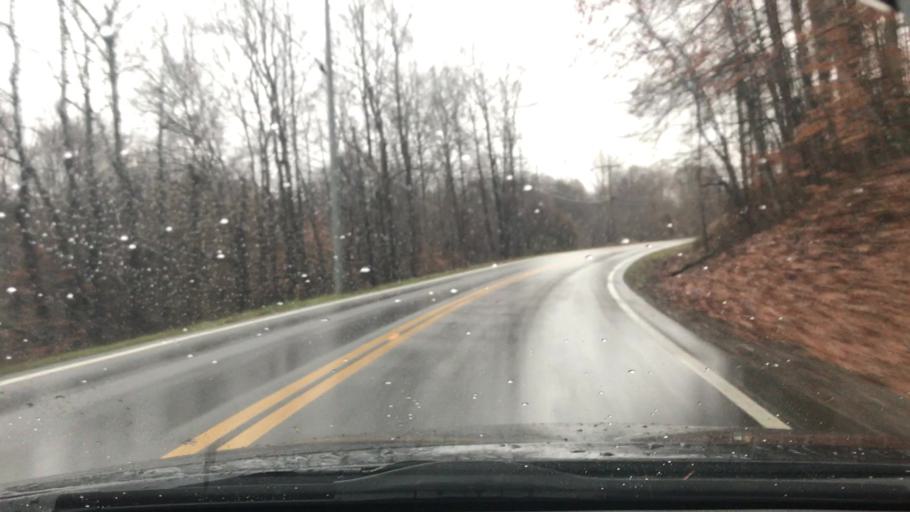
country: US
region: Tennessee
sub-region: Cheatham County
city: Ashland City
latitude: 36.2770
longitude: -87.1242
